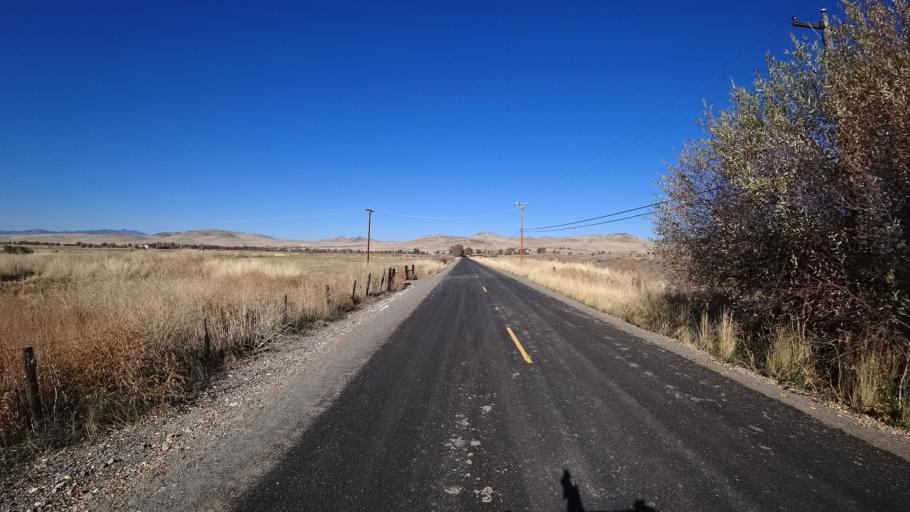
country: US
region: California
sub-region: Siskiyou County
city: Montague
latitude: 41.7172
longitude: -122.3892
